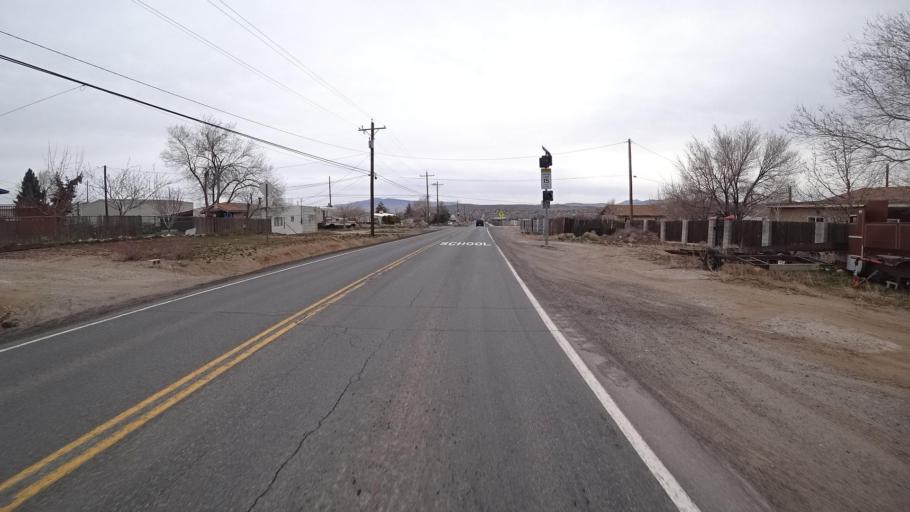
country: US
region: Nevada
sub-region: Washoe County
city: Sun Valley
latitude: 39.5999
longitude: -119.7865
